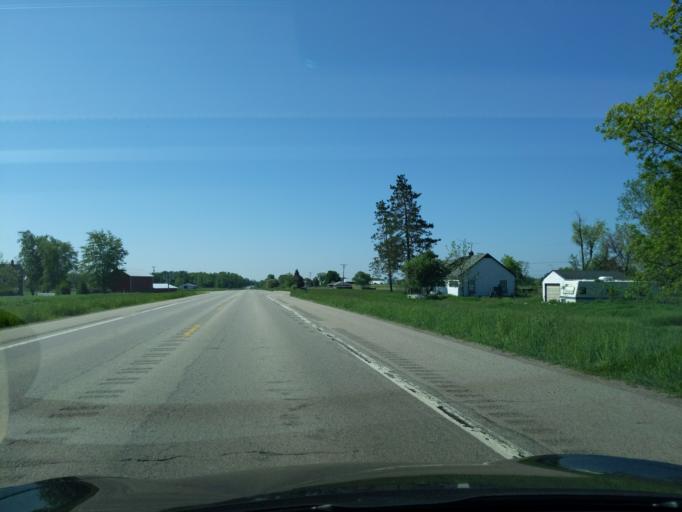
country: US
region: Michigan
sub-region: Ingham County
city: Stockbridge
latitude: 42.5253
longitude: -84.1906
